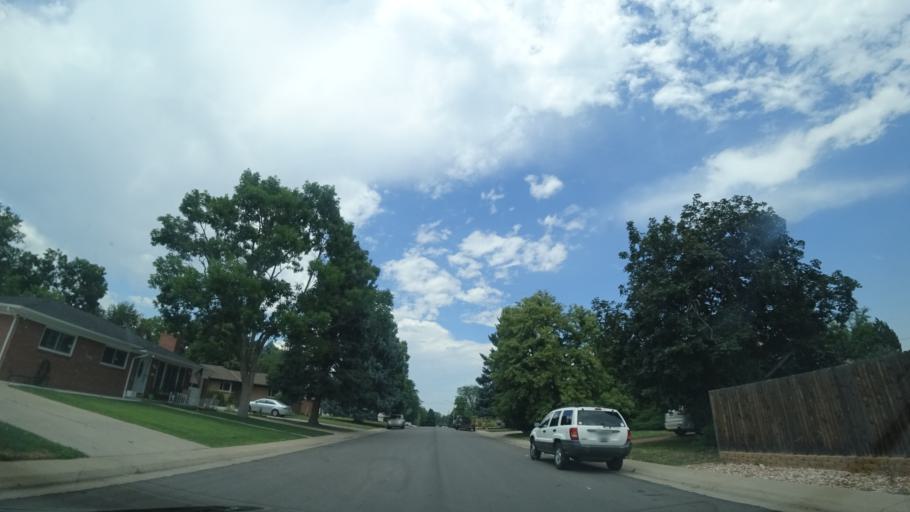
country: US
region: Colorado
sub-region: Jefferson County
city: Lakewood
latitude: 39.7187
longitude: -105.0940
